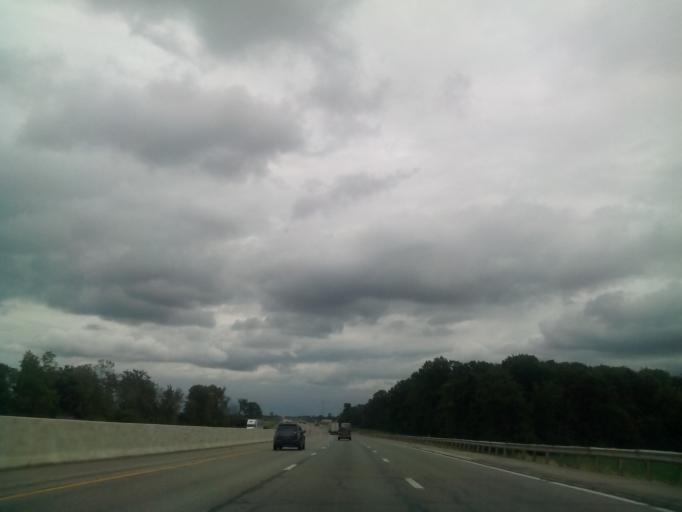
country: US
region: Ohio
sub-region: Wood County
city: Rossford
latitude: 41.5537
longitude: -83.5521
